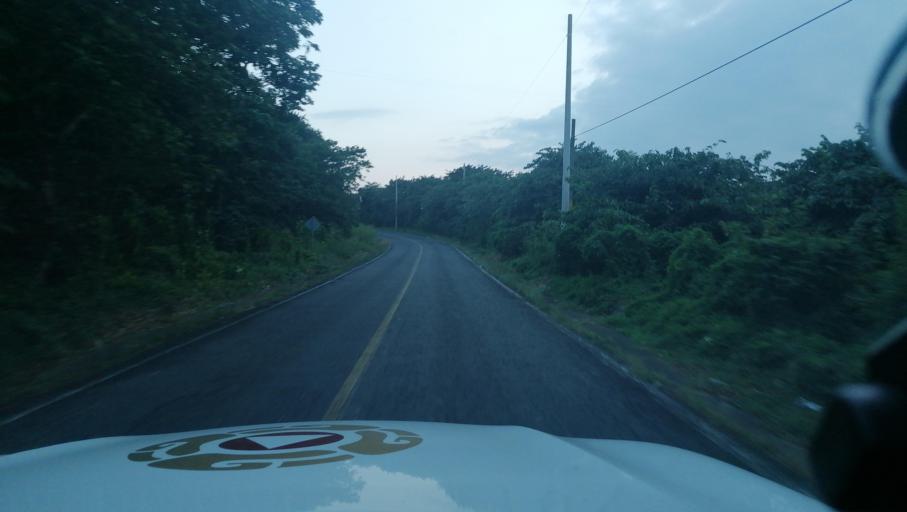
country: MX
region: Chiapas
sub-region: Cacahoatan
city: Benito Juarez
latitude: 15.0453
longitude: -92.2448
